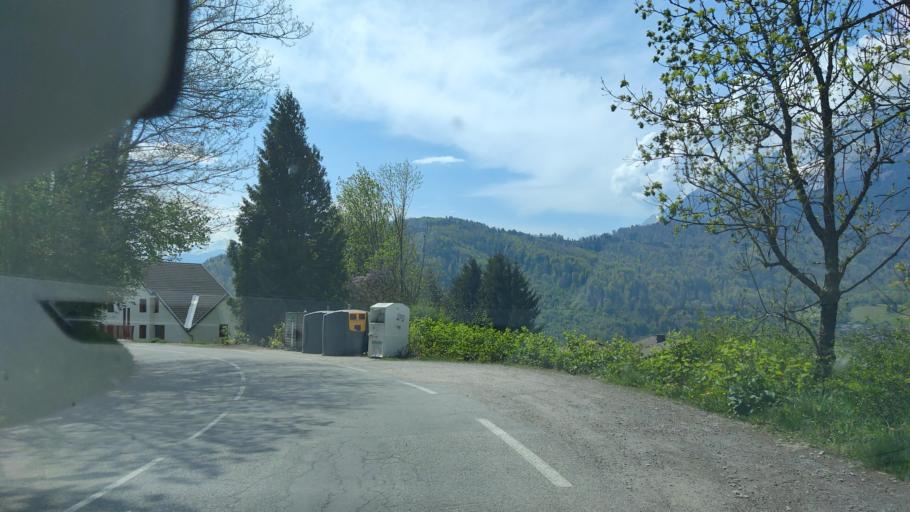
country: FR
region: Rhone-Alpes
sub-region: Departement de la Savoie
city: Ugine
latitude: 45.7590
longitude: 6.4197
